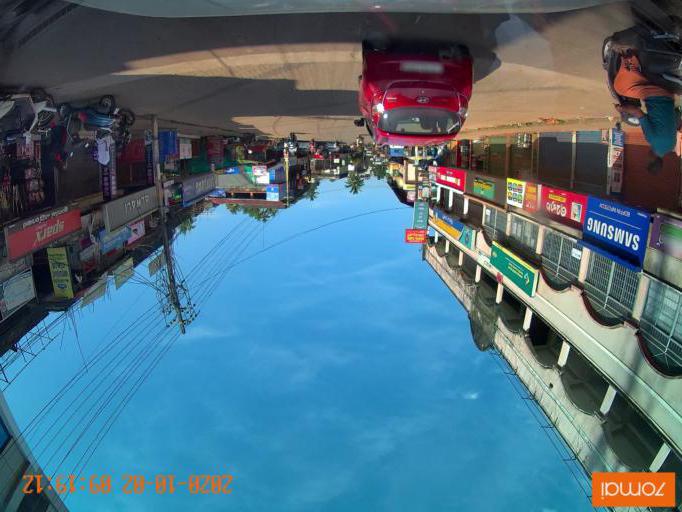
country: IN
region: Kerala
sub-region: Kozhikode
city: Naduvannur
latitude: 11.5621
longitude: 75.7575
